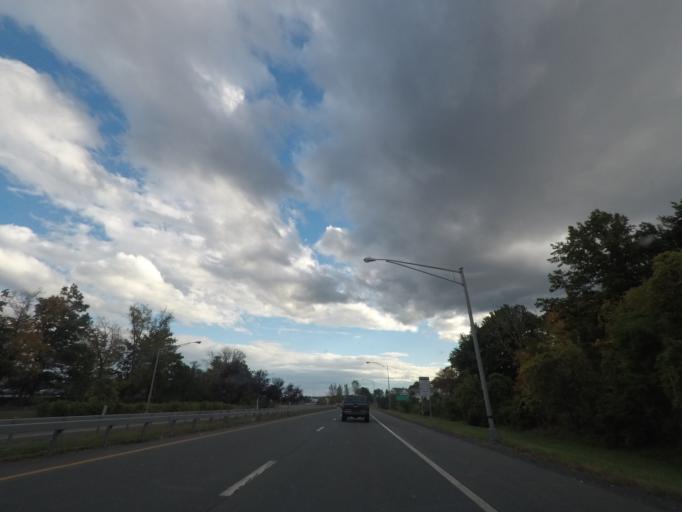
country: US
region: New York
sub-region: Albany County
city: McKownville
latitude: 42.6951
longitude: -73.8496
